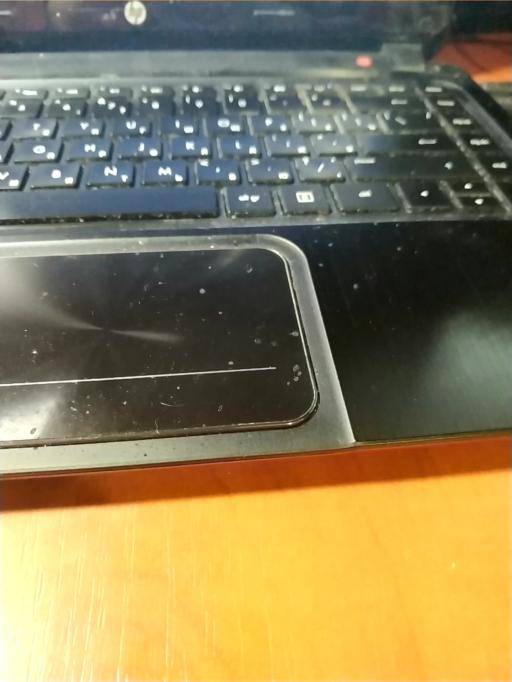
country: RU
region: Tverskaya
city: Likhoslavl'
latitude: 57.2722
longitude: 35.4063
